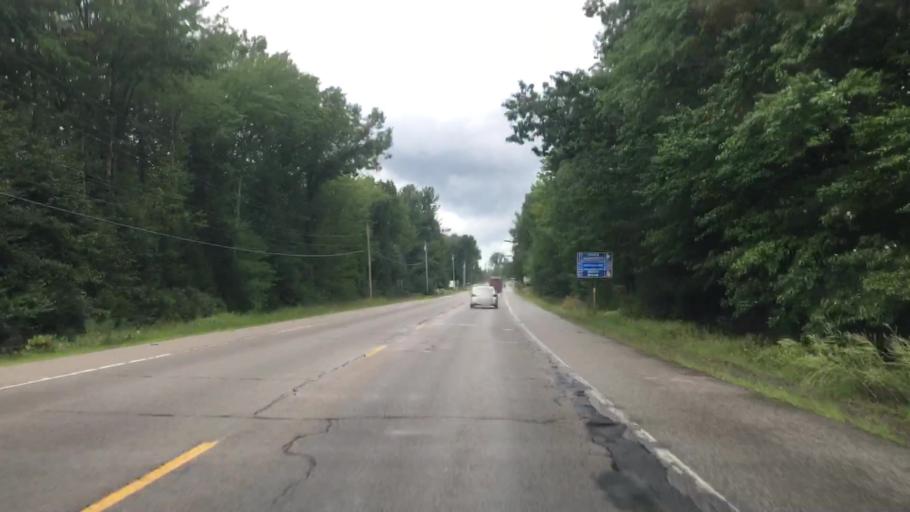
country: US
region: Maine
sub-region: York County
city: South Sanford
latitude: 43.4054
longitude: -70.7414
